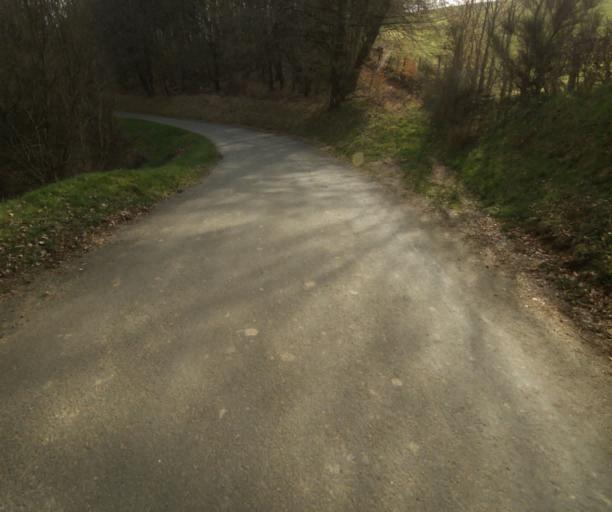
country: FR
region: Limousin
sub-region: Departement de la Correze
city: Naves
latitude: 45.3013
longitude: 1.7553
